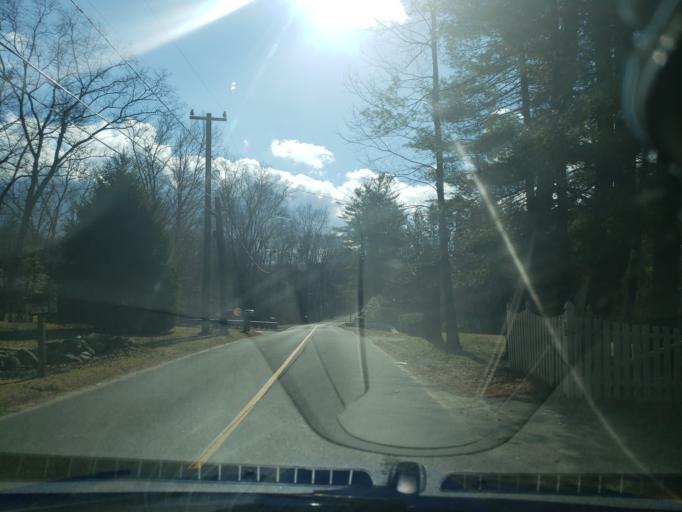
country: US
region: Connecticut
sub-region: Fairfield County
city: Bethel
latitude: 41.3842
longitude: -73.3766
